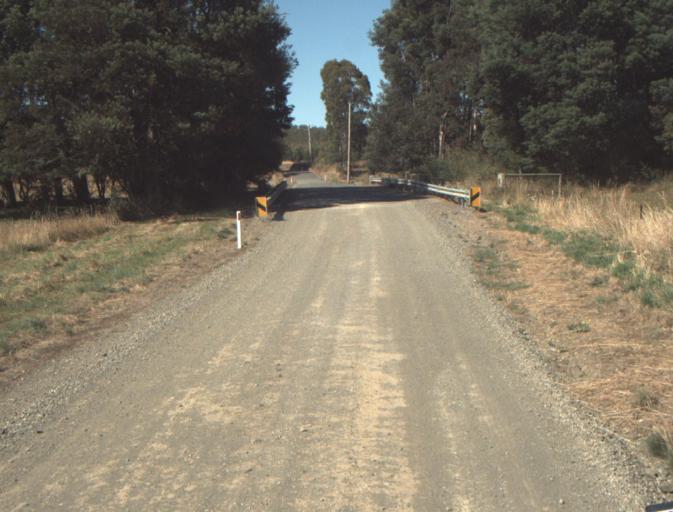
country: AU
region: Tasmania
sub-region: Launceston
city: Newstead
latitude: -41.3171
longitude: 147.3199
